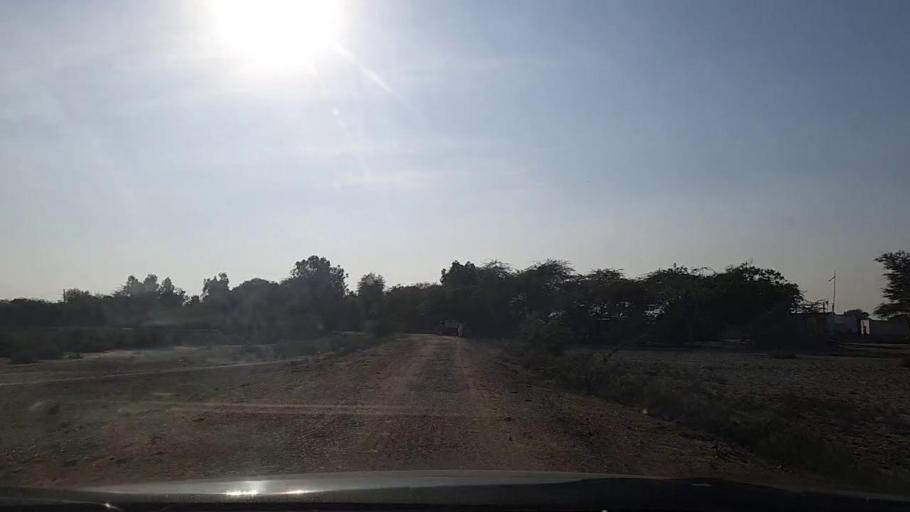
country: PK
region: Sindh
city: Mirpur Sakro
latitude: 24.5337
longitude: 67.6339
